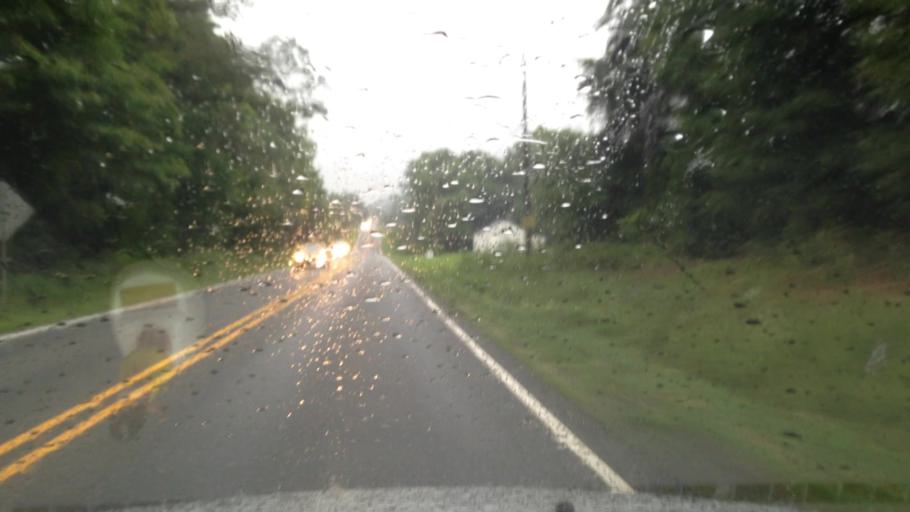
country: US
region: North Carolina
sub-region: Forsyth County
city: Walkertown
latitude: 36.1610
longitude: -80.1323
